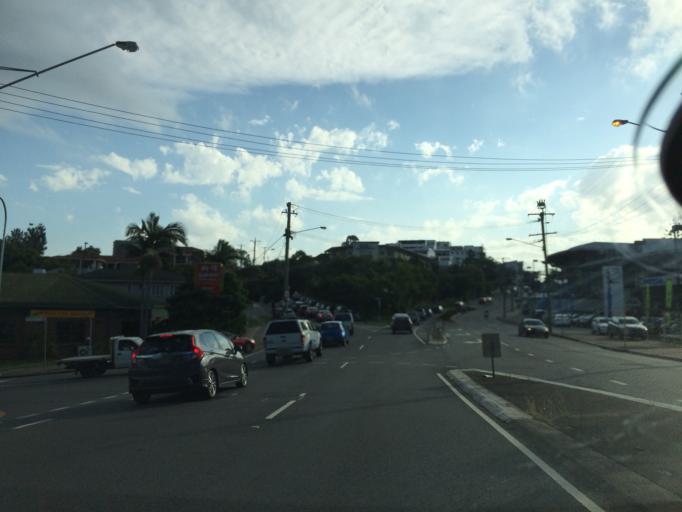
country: AU
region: Queensland
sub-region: Brisbane
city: Taringa
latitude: -27.4913
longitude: 152.9837
